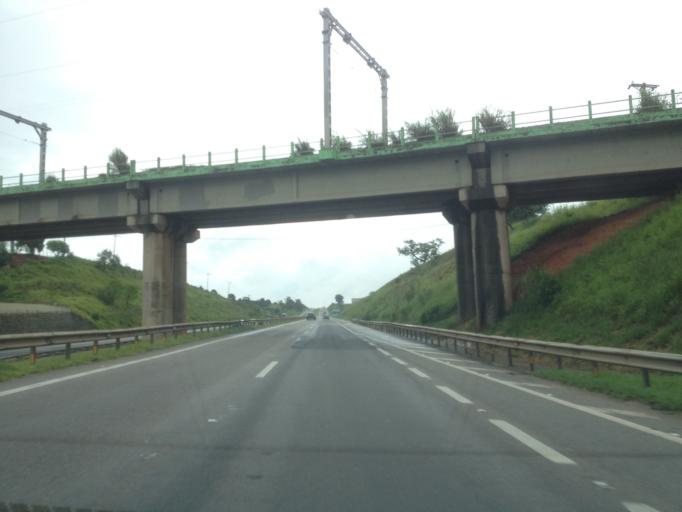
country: BR
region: Sao Paulo
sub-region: Itu
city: Itu
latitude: -23.3624
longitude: -47.3260
